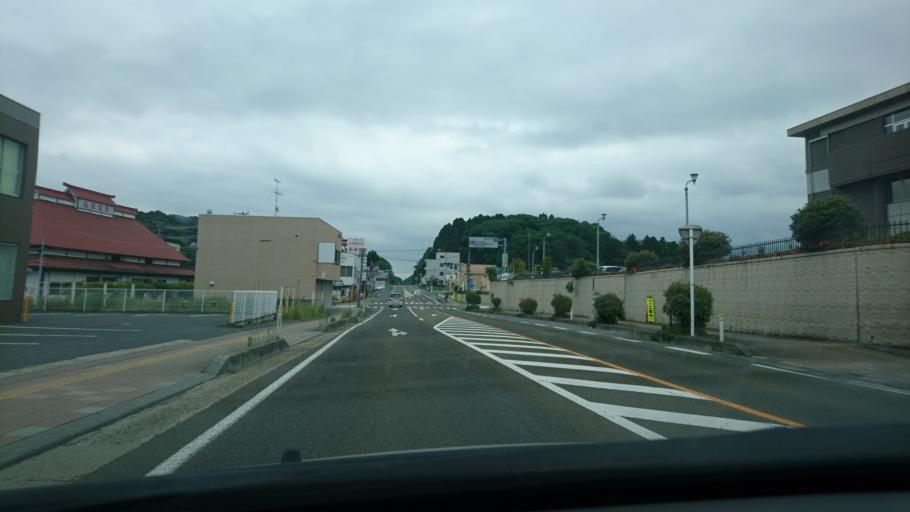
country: JP
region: Miyagi
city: Furukawa
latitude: 38.7303
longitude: 141.0223
